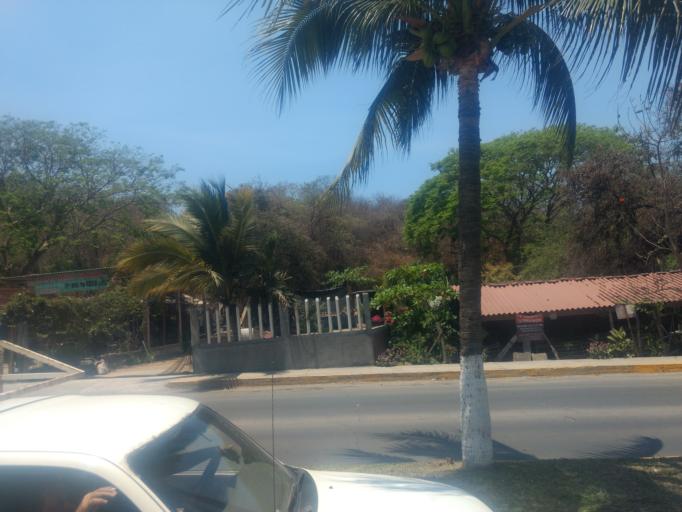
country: MX
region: Colima
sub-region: Manzanillo
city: Manzanillo
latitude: 19.1159
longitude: -104.3500
